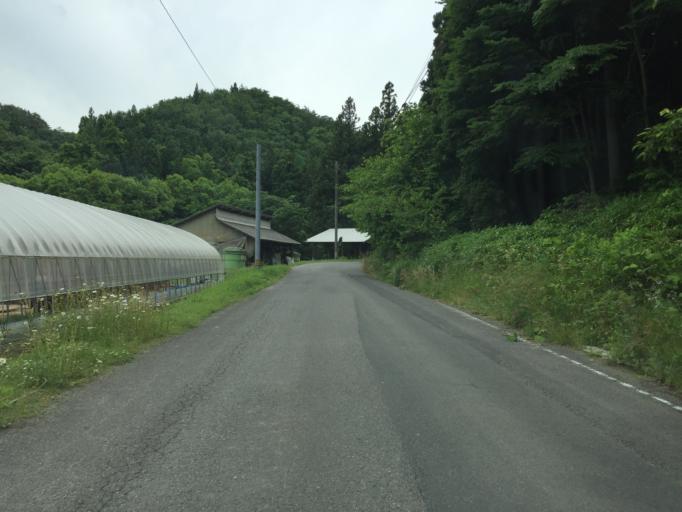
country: JP
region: Fukushima
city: Funehikimachi-funehiki
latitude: 37.4379
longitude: 140.7899
